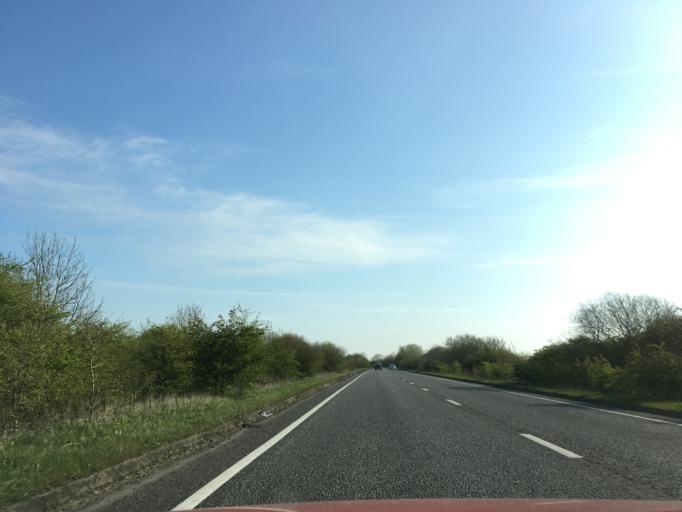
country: GB
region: England
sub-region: Northamptonshire
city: Deanshanger
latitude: 52.0463
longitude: -0.8800
